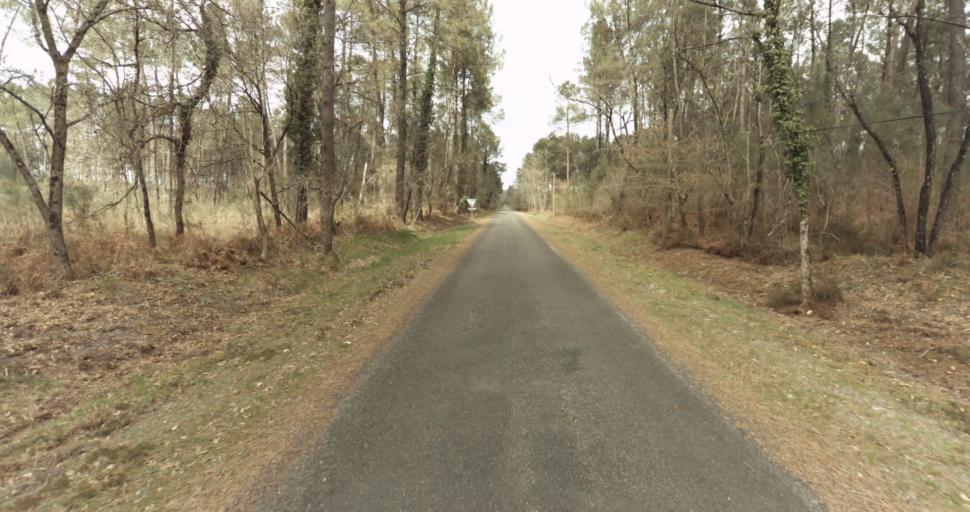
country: FR
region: Aquitaine
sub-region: Departement des Landes
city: Roquefort
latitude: 44.0533
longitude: -0.3780
